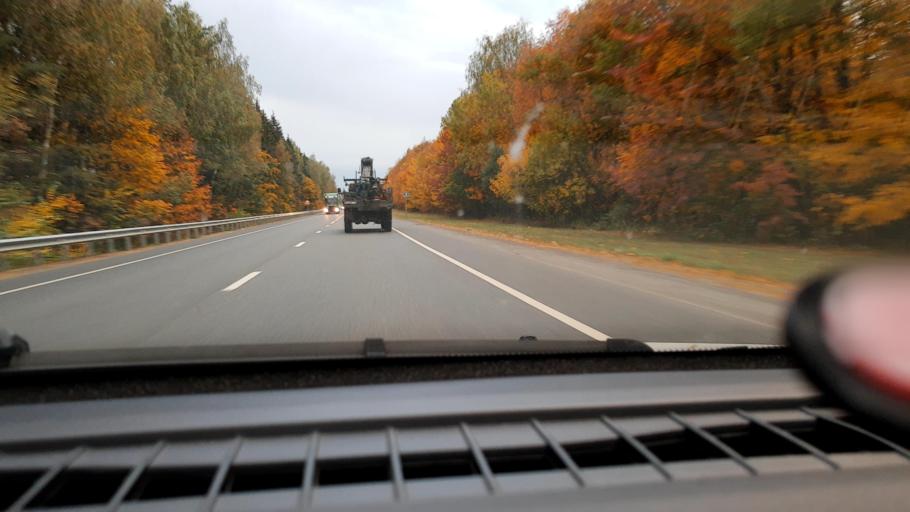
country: RU
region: Vladimir
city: Orgtrud
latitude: 56.1996
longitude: 40.8223
